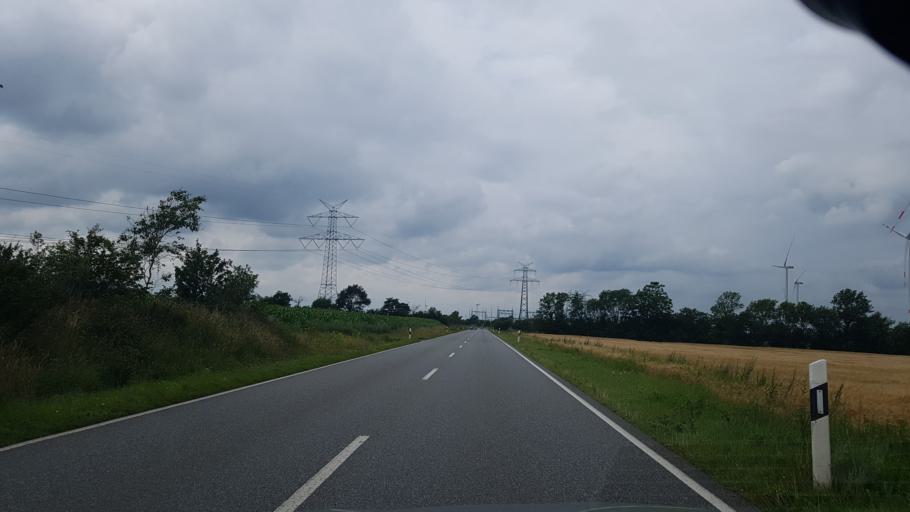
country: DE
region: Schleswig-Holstein
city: Jardelund
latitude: 54.8445
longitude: 9.2056
